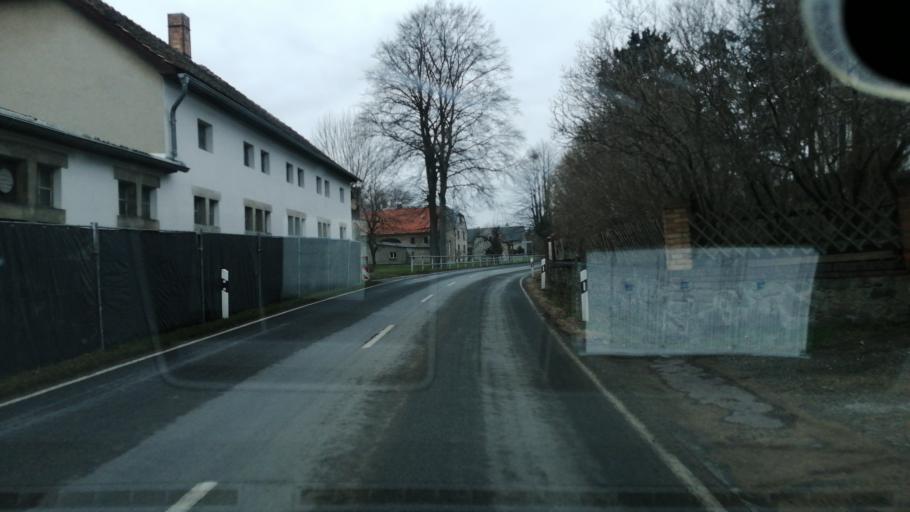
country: DE
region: Saxony
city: Sohland am Rotstein
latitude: 51.0678
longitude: 14.7823
